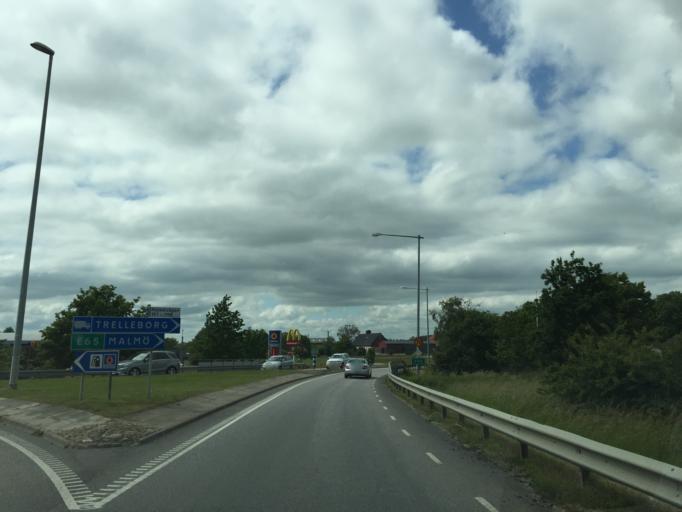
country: SE
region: Skane
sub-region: Ystads Kommun
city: Ystad
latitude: 55.4385
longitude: 13.7930
